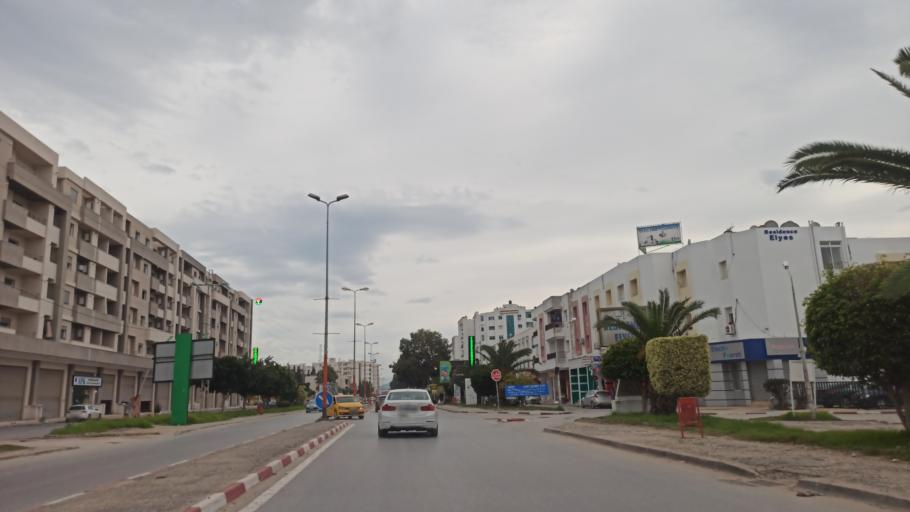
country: TN
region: Ariana
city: Ariana
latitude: 36.8635
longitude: 10.2532
